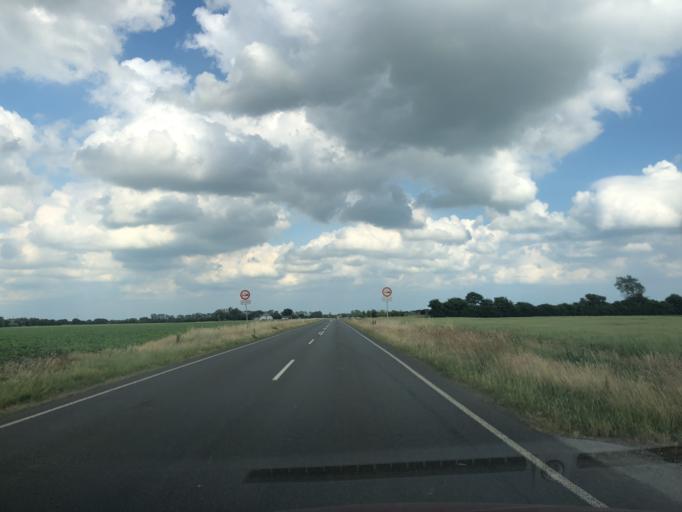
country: DK
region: Zealand
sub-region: Stevns Kommune
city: Harlev
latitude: 55.3162
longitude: 12.1927
